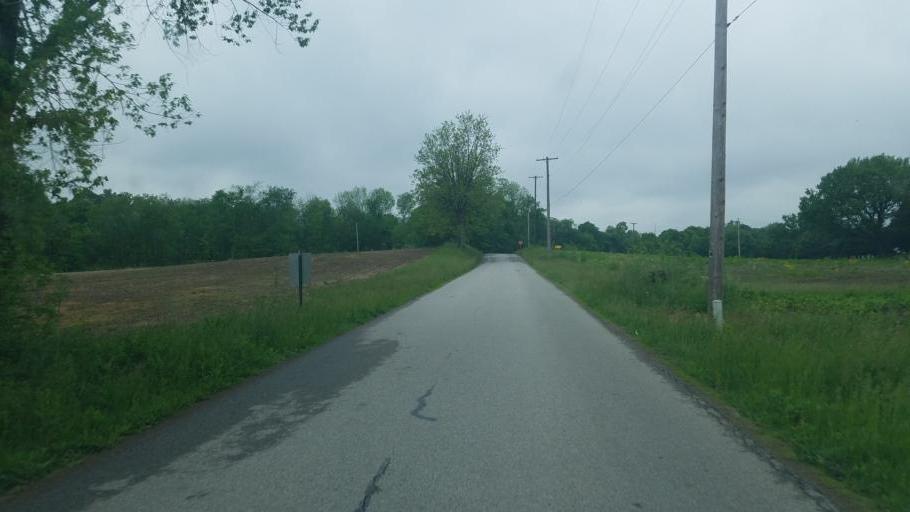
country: US
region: Ohio
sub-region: Richland County
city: Lincoln Heights
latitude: 40.7232
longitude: -82.4434
